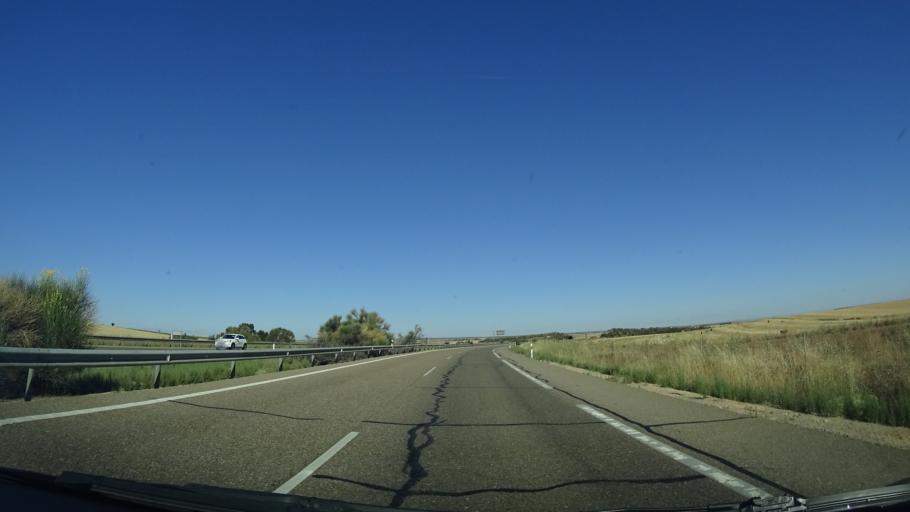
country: ES
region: Castille and Leon
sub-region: Provincia de Valladolid
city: Villardefrades
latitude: 41.7319
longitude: -5.2596
